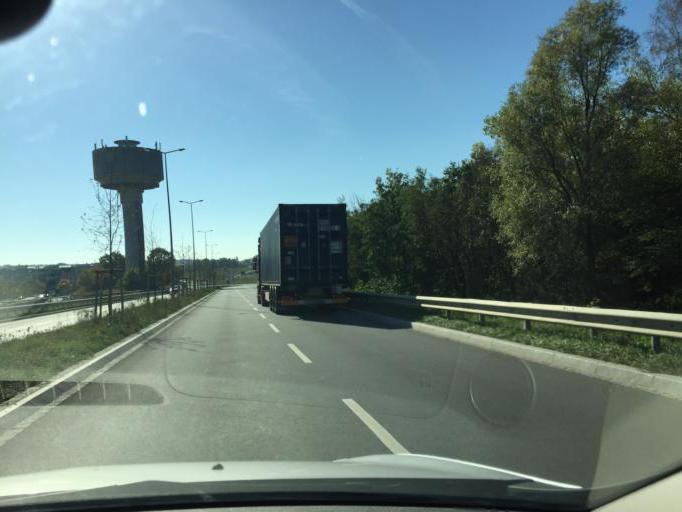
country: LU
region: Luxembourg
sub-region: Canton de Luxembourg
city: Sandweiler
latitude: 49.5988
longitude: 6.2125
